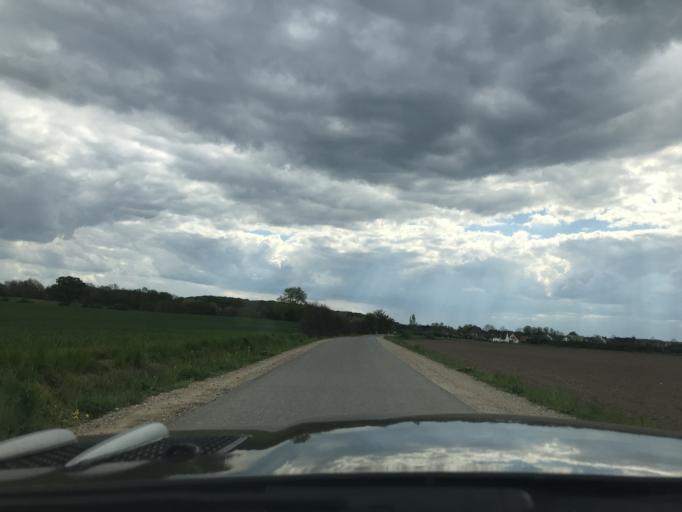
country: DE
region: Schleswig-Holstein
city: Gross Gronau
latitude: 53.7730
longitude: 10.7773
